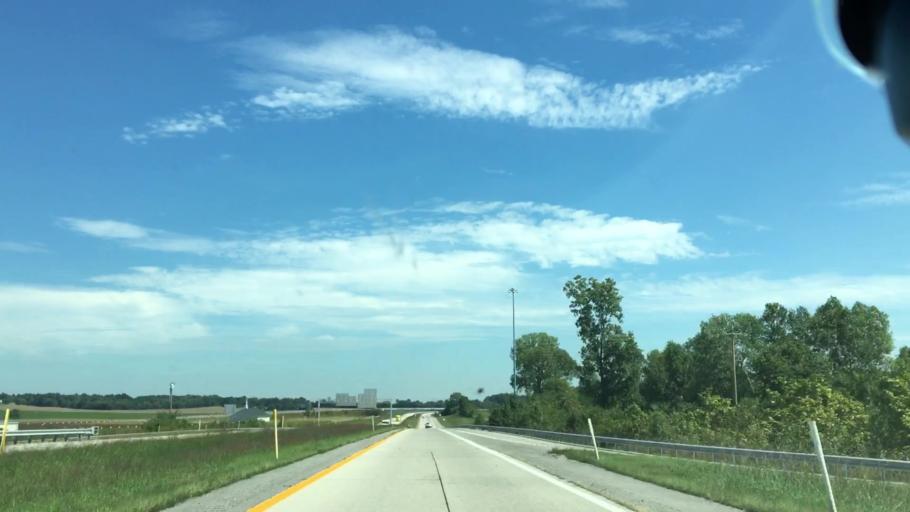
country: US
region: Kentucky
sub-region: Henderson County
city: Henderson
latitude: 37.8098
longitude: -87.5621
